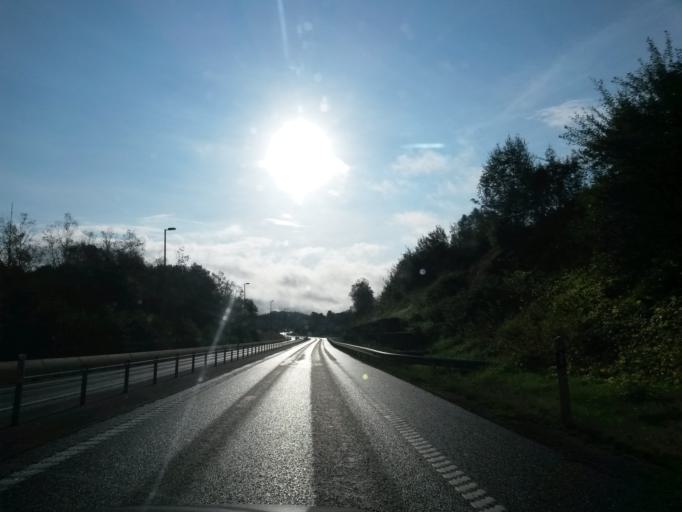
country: SE
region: Vaestra Goetaland
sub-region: Boras Kommun
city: Boras
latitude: 57.6808
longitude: 12.9529
